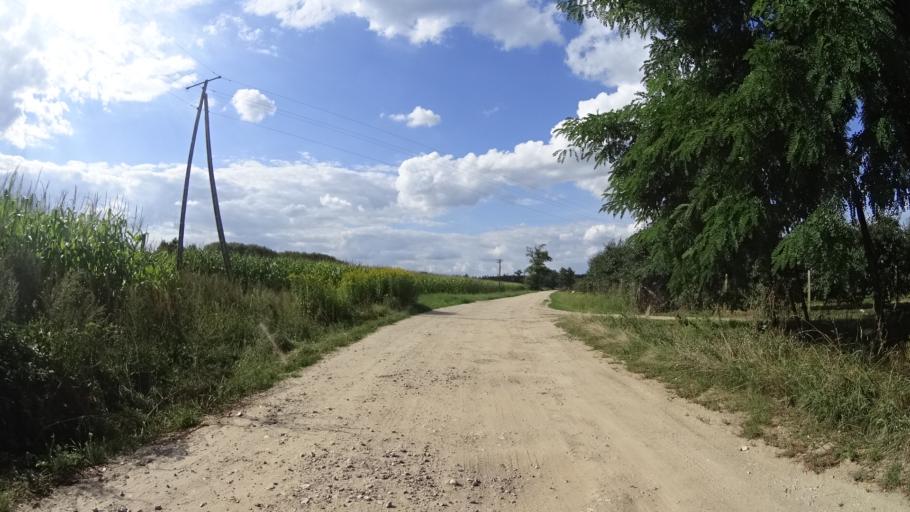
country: PL
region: Masovian Voivodeship
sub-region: Powiat grojecki
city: Mogielnica
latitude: 51.6780
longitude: 20.7659
